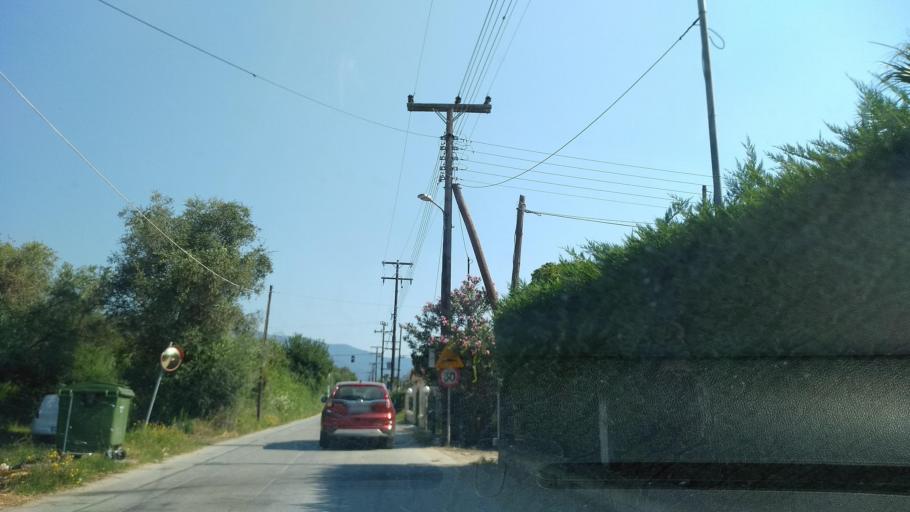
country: GR
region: Central Macedonia
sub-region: Nomos Thessalonikis
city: Nea Vrasna
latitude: 40.6887
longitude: 23.6890
